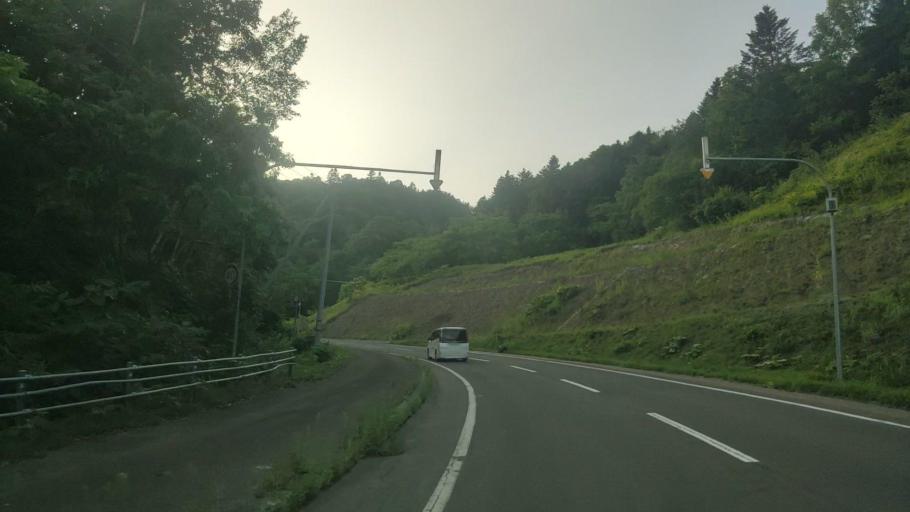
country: JP
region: Hokkaido
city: Bibai
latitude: 43.2374
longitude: 142.0366
